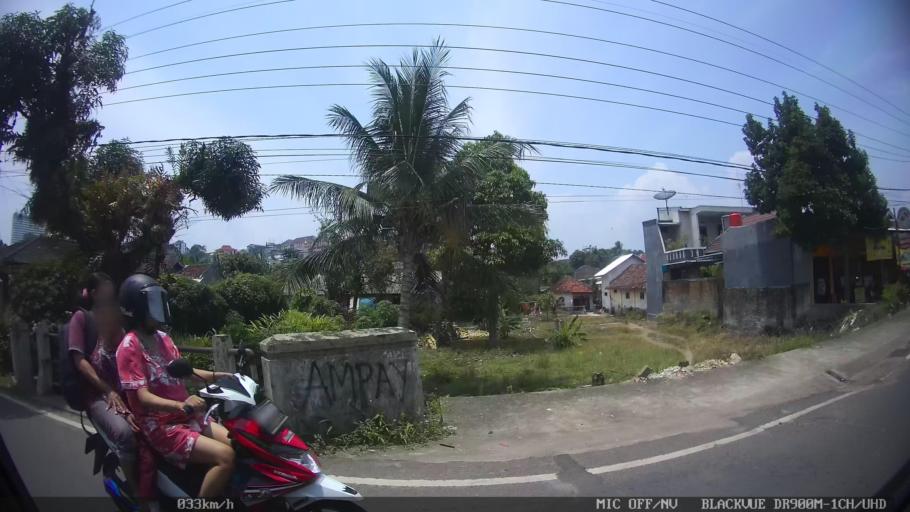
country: ID
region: Lampung
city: Bandarlampung
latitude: -5.4463
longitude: 105.2558
